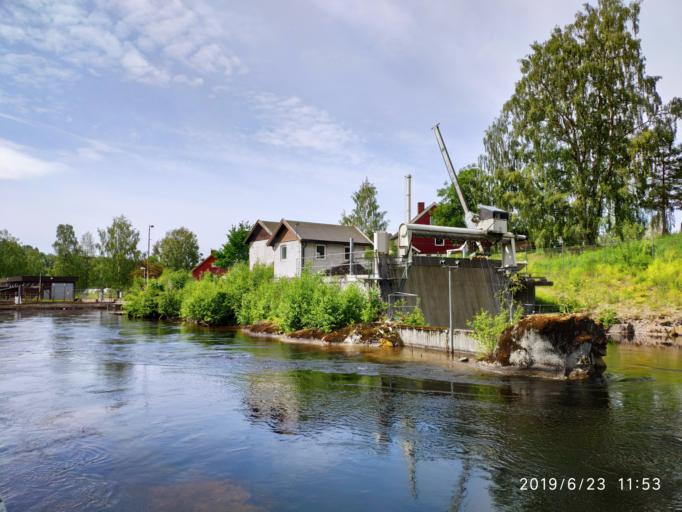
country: NO
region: Oppland
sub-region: Jevnaker
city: Jevnaker
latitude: 60.2044
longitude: 10.3416
